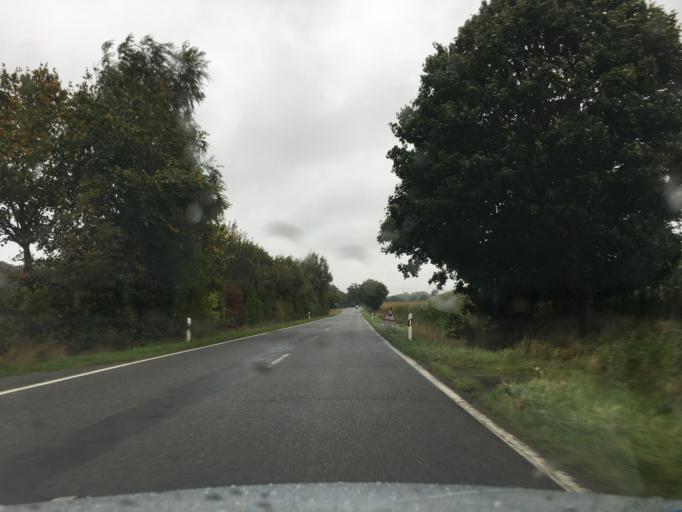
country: DE
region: Schleswig-Holstein
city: Felm
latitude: 54.3874
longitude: 10.0570
